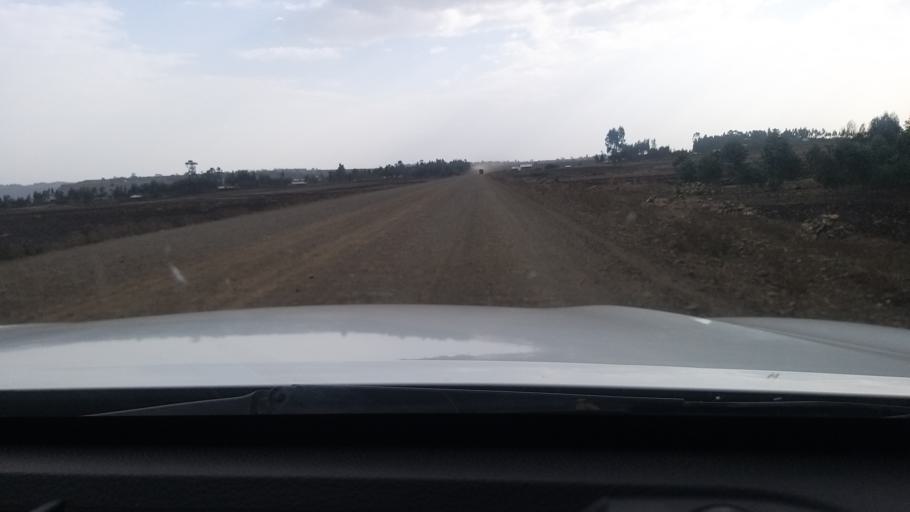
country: ET
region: Amhara
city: Were Ilu
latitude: 10.4525
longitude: 39.2091
